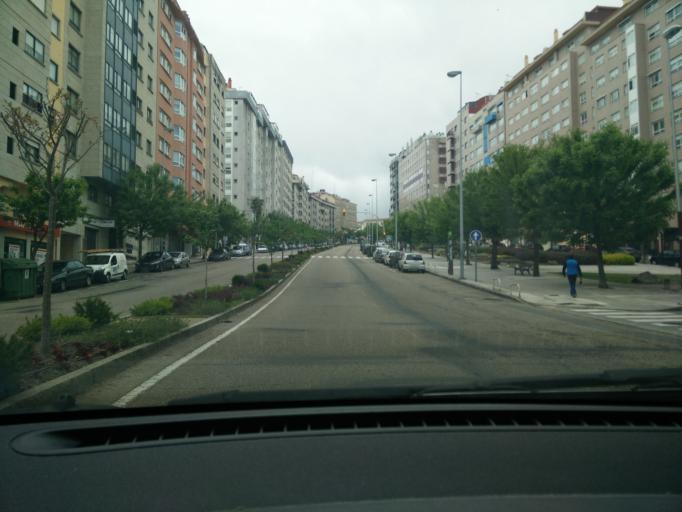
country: ES
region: Galicia
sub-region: Provincia de Pontevedra
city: Vigo
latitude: 42.2149
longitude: -8.7423
